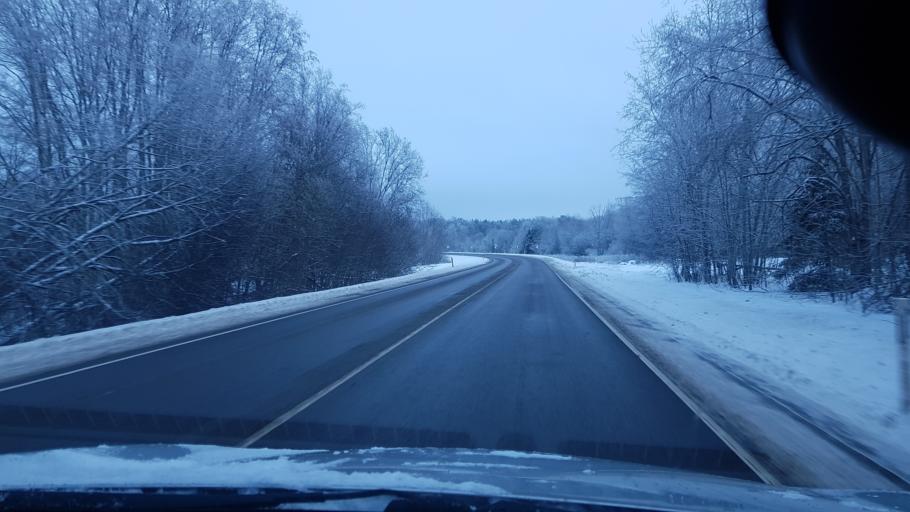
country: EE
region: Harju
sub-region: Paldiski linn
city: Paldiski
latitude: 59.3408
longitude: 24.2002
